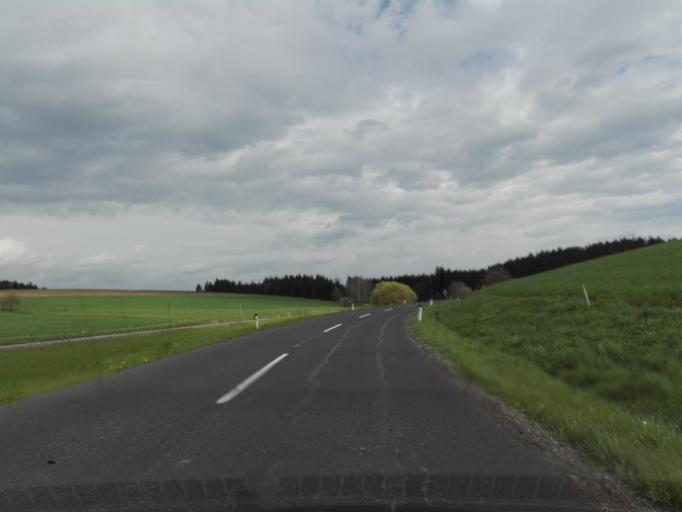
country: AT
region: Upper Austria
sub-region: Politischer Bezirk Rohrbach
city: Kleinzell im Muehlkreis
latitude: 48.4703
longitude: 14.0182
